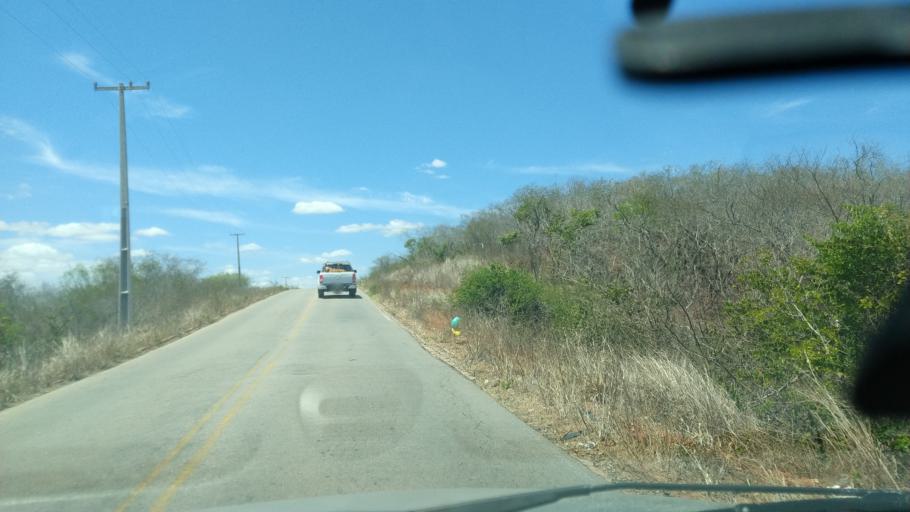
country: BR
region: Rio Grande do Norte
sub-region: Sao Paulo Do Potengi
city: Sao Paulo do Potengi
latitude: -5.9068
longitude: -35.6047
